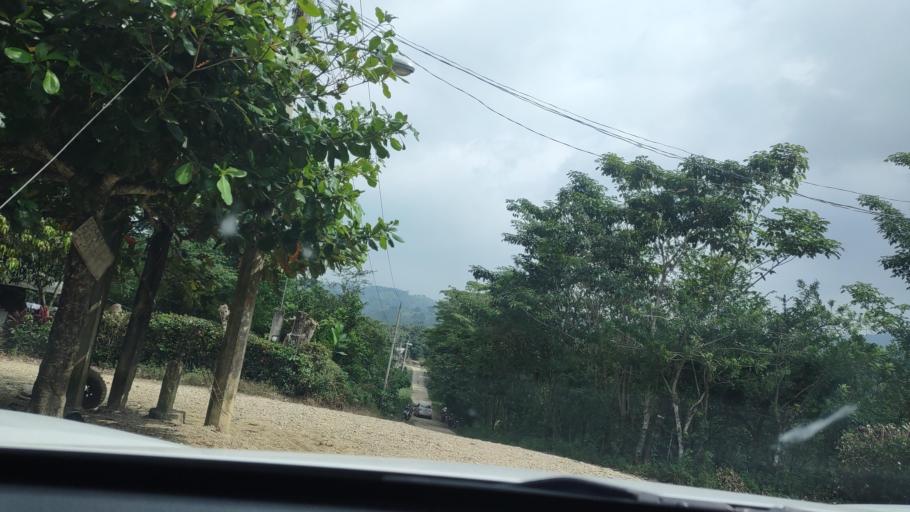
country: MX
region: Veracruz
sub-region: Uxpanapa
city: Poblado 10
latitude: 17.5219
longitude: -94.3035
